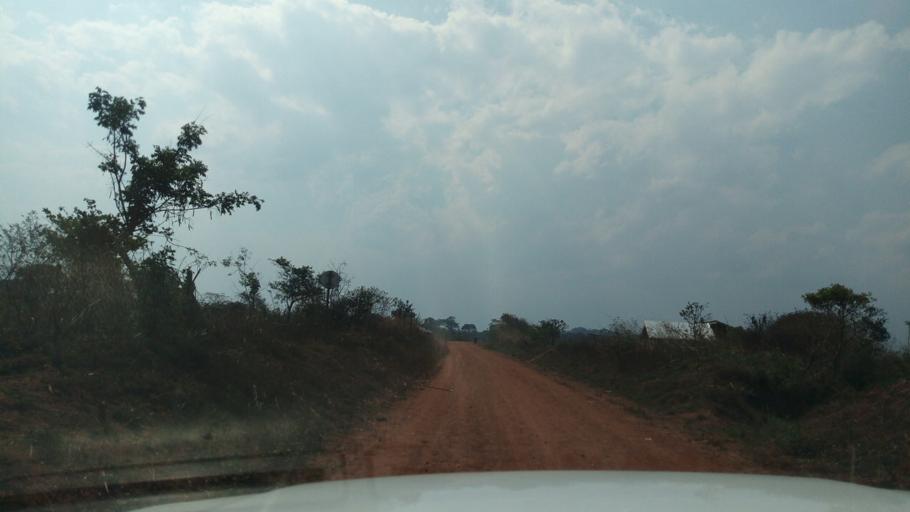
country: CD
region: Katanga
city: Kalemie
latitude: -5.5206
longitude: 28.9818
